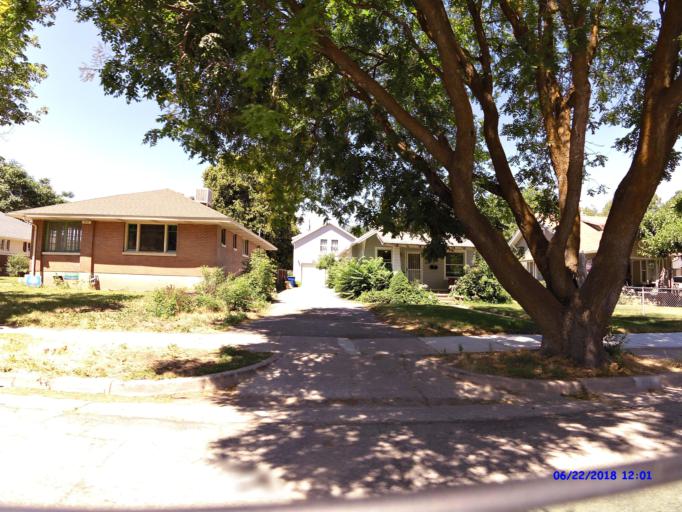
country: US
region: Utah
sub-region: Weber County
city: Ogden
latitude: 41.2377
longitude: -111.9715
